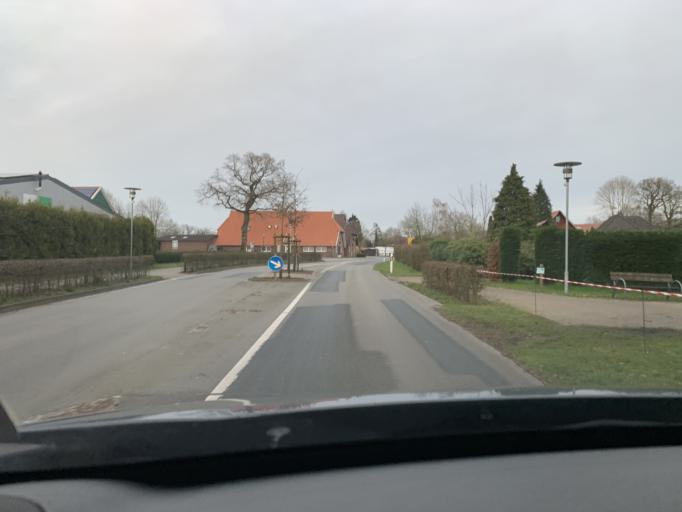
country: DE
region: Lower Saxony
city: Apen
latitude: 53.1756
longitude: 7.8201
